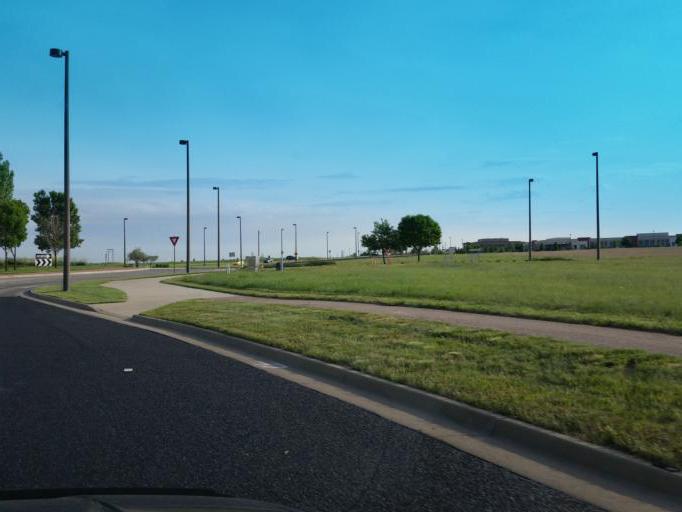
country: US
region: Colorado
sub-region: Larimer County
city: Loveland
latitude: 40.4254
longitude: -105.0020
